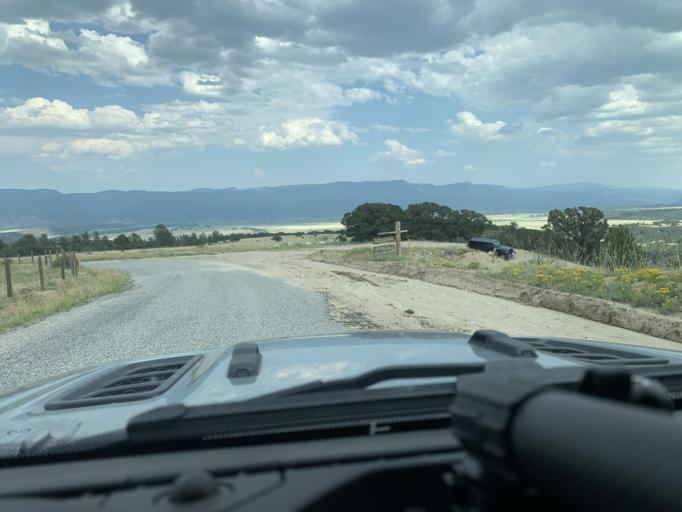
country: US
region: Colorado
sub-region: Chaffee County
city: Buena Vista
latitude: 38.7391
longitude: -106.1655
